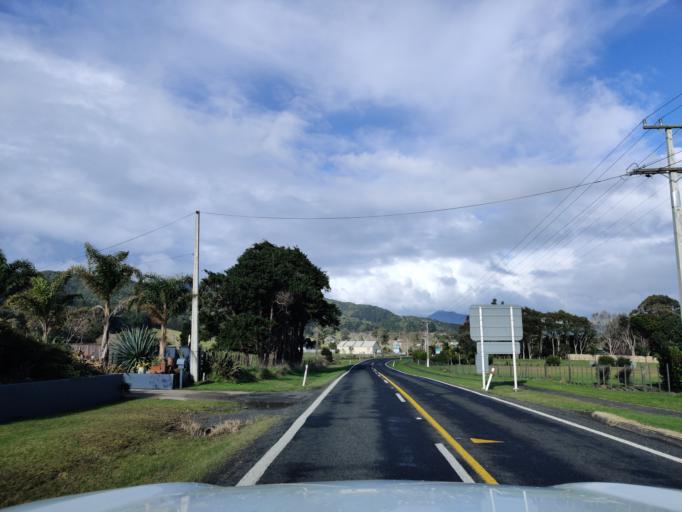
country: NZ
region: Waikato
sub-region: Thames-Coromandel District
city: Coromandel
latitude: -36.7640
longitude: 175.5021
